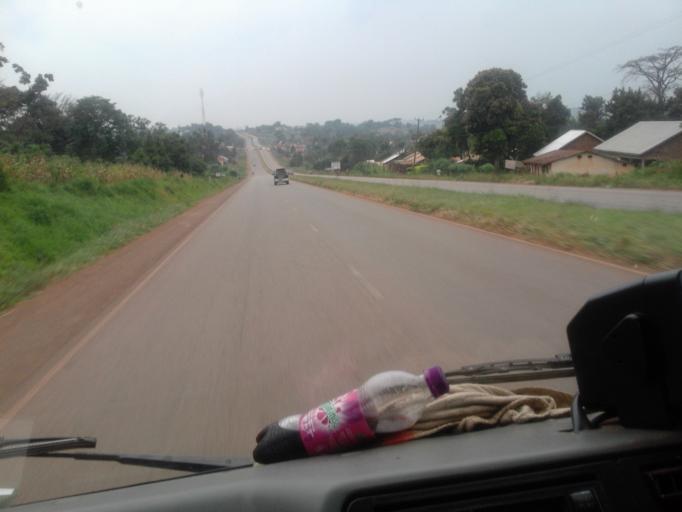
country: UG
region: Eastern Region
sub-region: Jinja District
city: Bugembe
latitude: 0.4738
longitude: 33.2585
